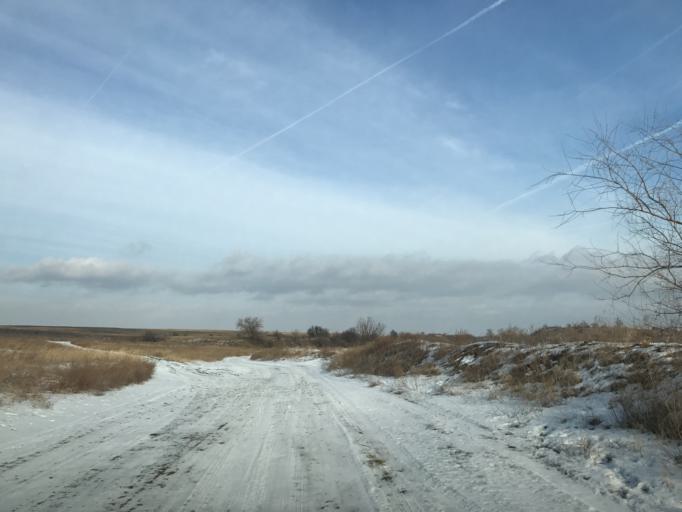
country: RU
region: Rostov
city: Staraya Stanitsa
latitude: 48.2454
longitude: 40.3991
